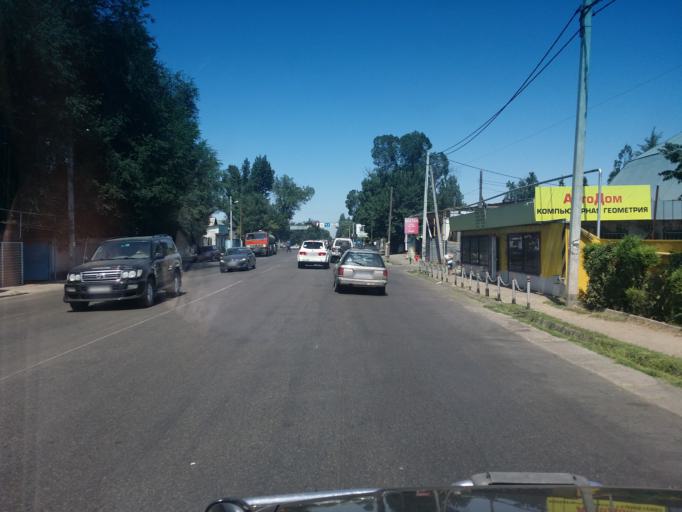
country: KZ
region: Almaty Oblysy
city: Pervomayskiy
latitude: 43.3155
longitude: 76.9302
